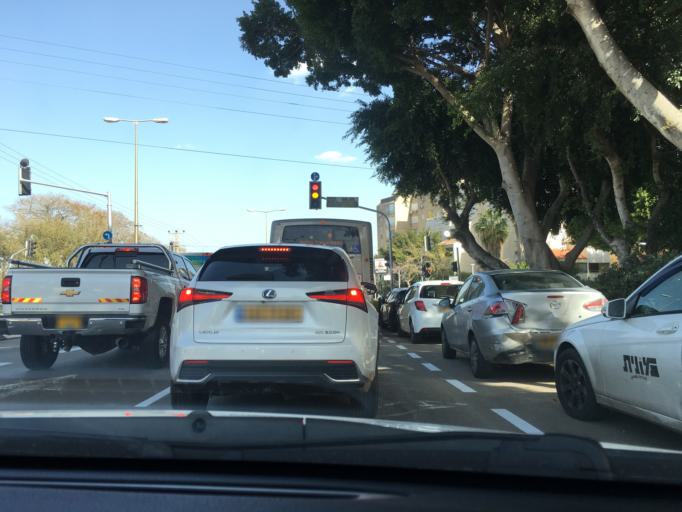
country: IL
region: Central District
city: Kfar Saba
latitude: 32.1804
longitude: 34.8970
